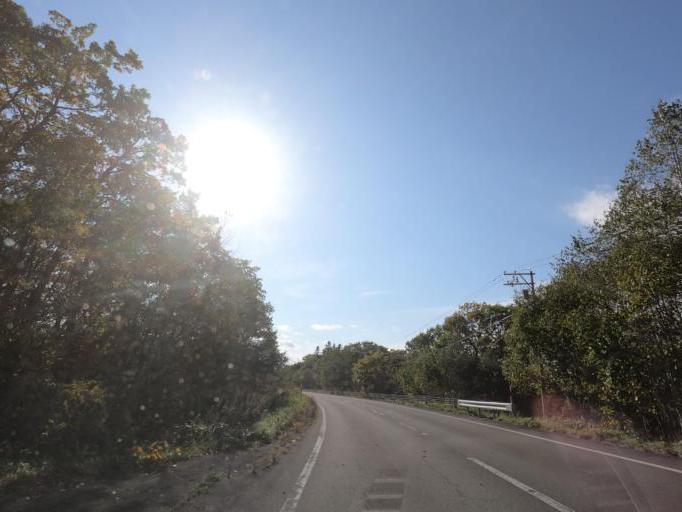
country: JP
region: Hokkaido
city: Obihiro
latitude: 42.6131
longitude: 143.4653
